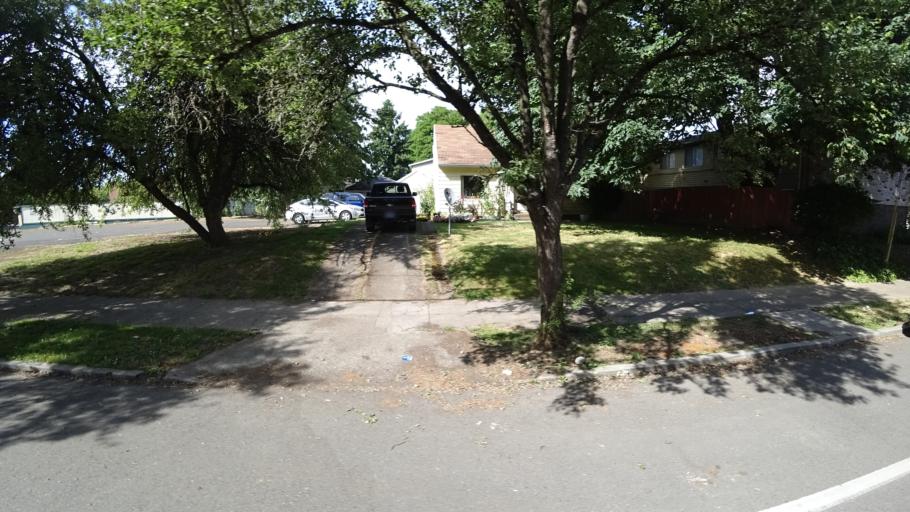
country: US
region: Washington
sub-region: Clark County
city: Vancouver
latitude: 45.5924
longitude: -122.7310
